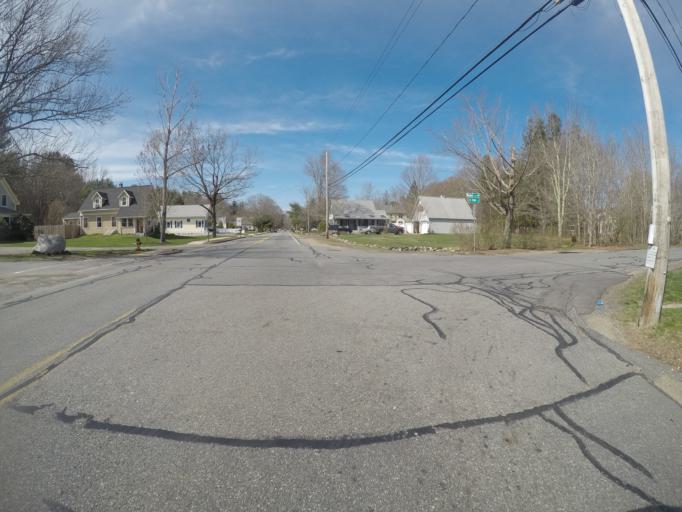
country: US
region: Massachusetts
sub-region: Bristol County
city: Easton
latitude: 42.0372
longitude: -71.0675
